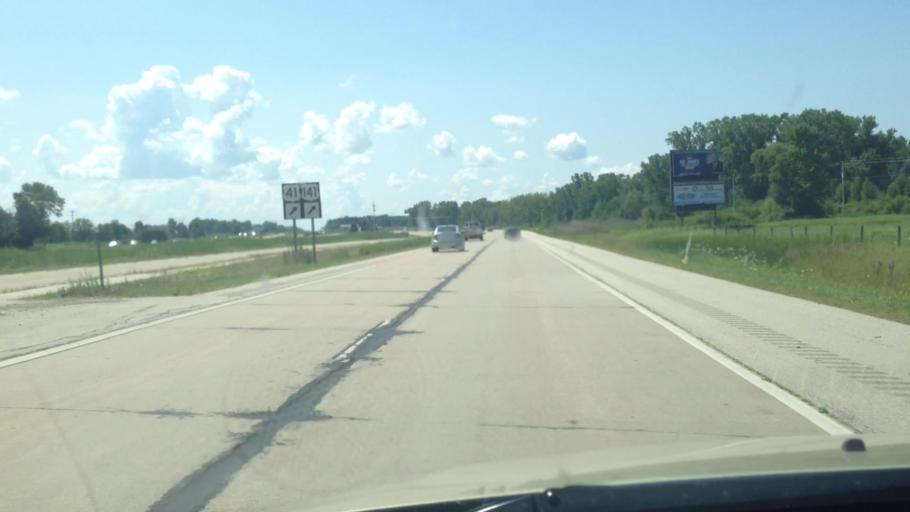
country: US
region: Wisconsin
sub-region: Brown County
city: Suamico
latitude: 44.7480
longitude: -88.0513
